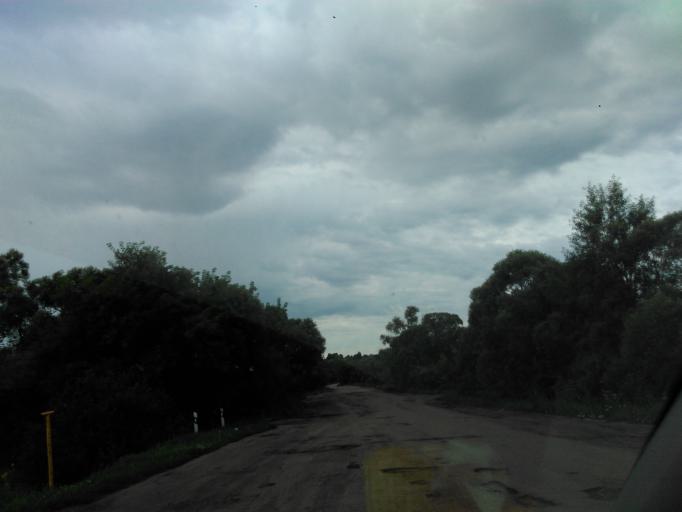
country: RU
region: Penza
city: Belinskiy
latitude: 52.9771
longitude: 43.4364
